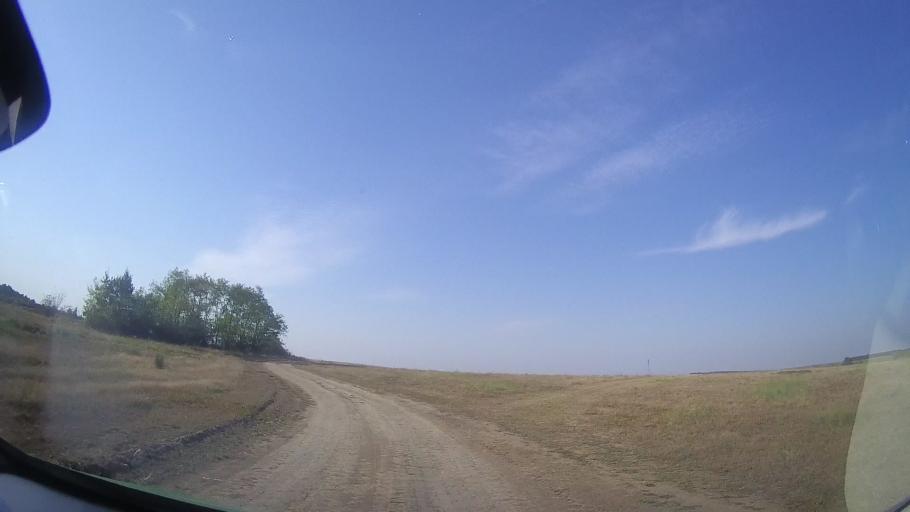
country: RO
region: Timis
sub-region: Comuna Bogda
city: Bogda
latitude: 45.8857
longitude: 21.5566
